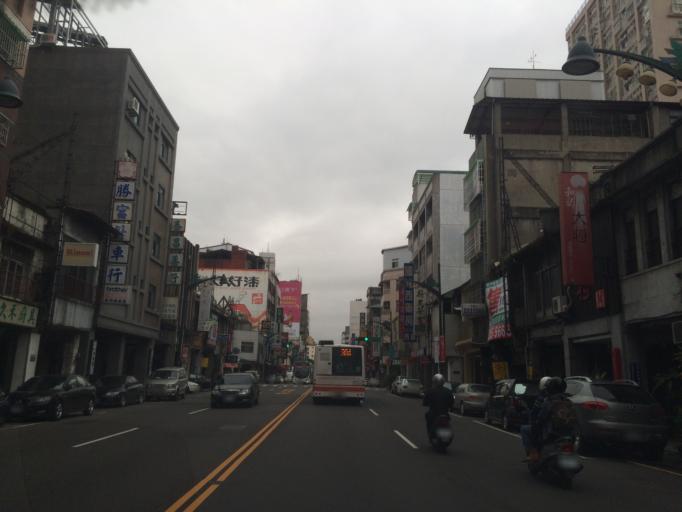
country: TW
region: Taiwan
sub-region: Taichung City
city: Taichung
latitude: 24.1460
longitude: 120.6754
